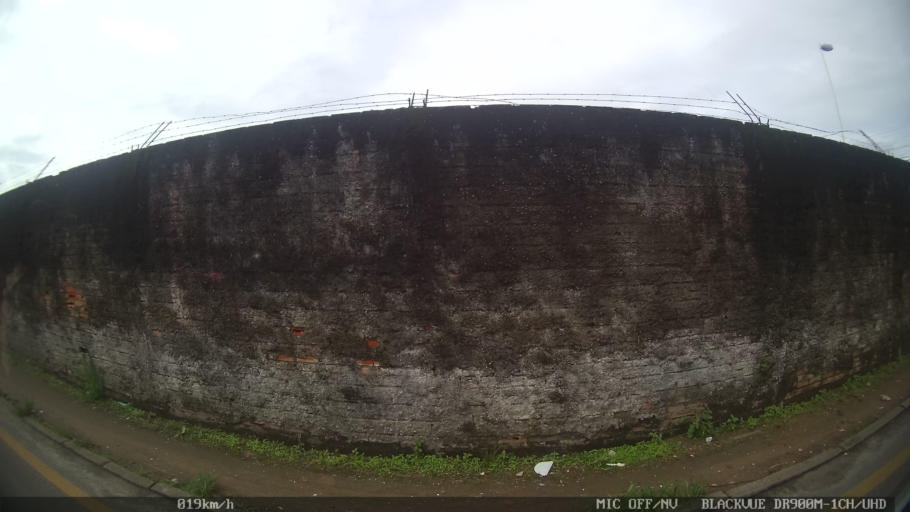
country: BR
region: Santa Catarina
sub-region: Sao Jose
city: Campinas
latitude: -27.5574
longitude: -48.6233
